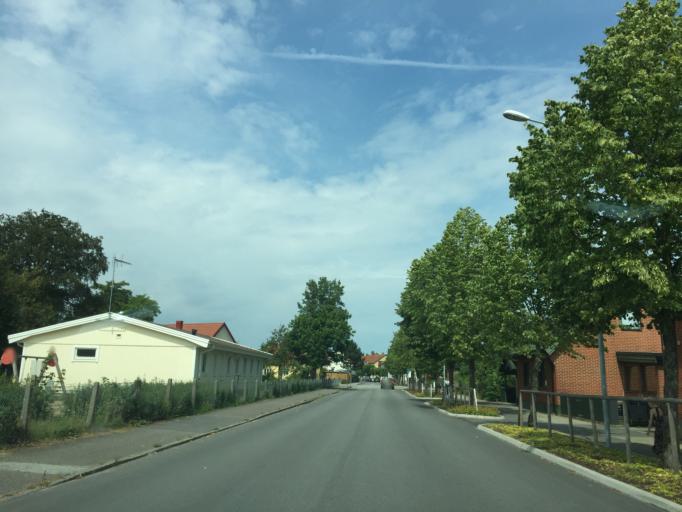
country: SE
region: Skane
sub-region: Sjobo Kommun
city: Sjoebo
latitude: 55.6336
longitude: 13.7106
